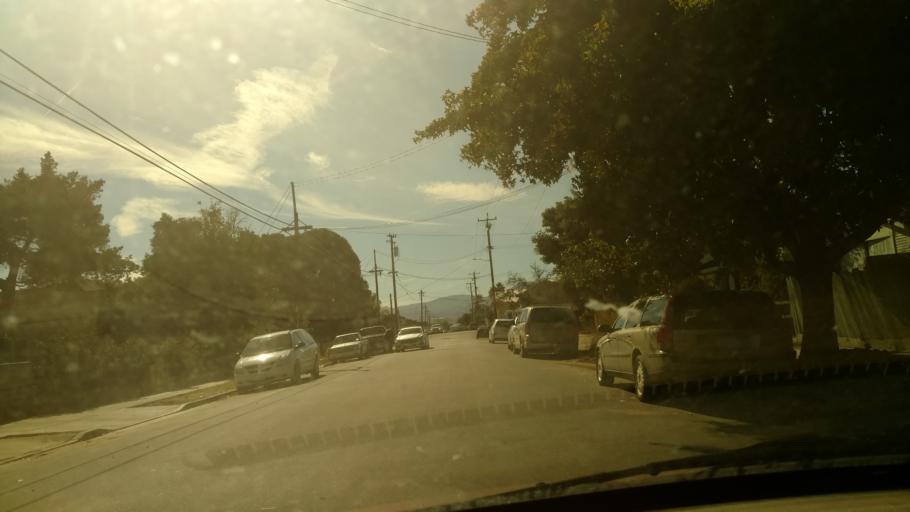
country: US
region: California
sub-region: San Benito County
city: Hollister
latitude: 36.8555
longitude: -121.4009
